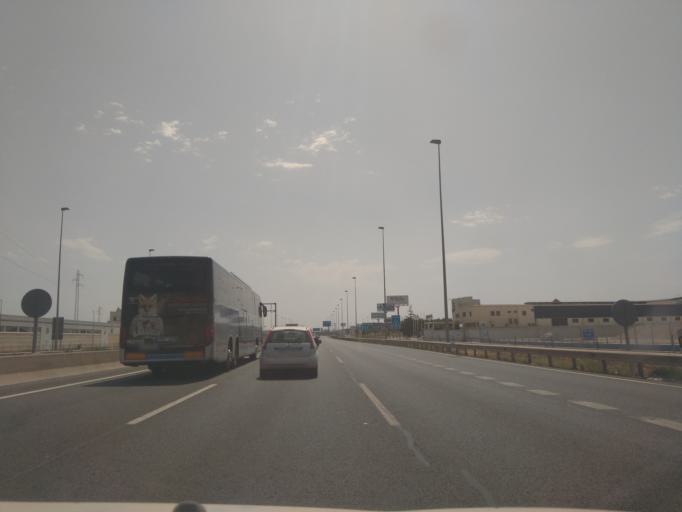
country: ES
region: Valencia
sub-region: Provincia de Valencia
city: Catarroja
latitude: 39.3862
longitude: -0.3966
